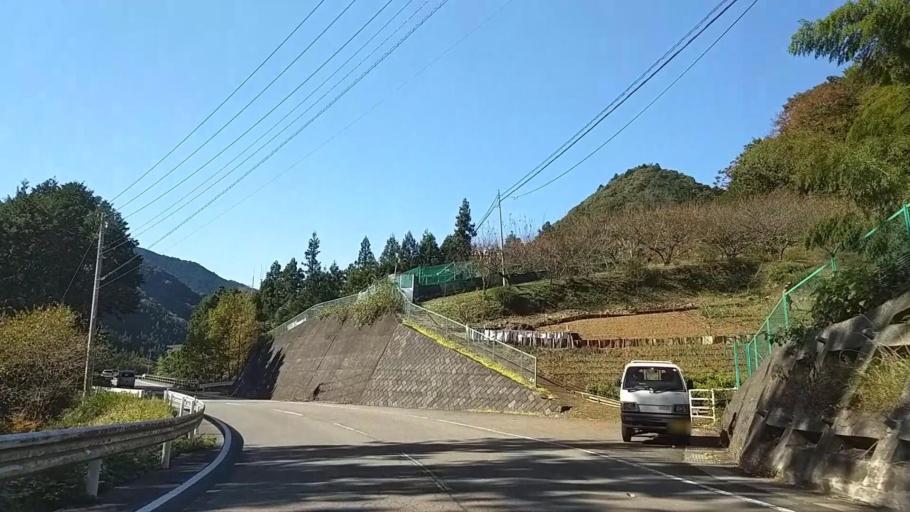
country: JP
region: Yamanashi
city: Uenohara
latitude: 35.6796
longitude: 139.0732
